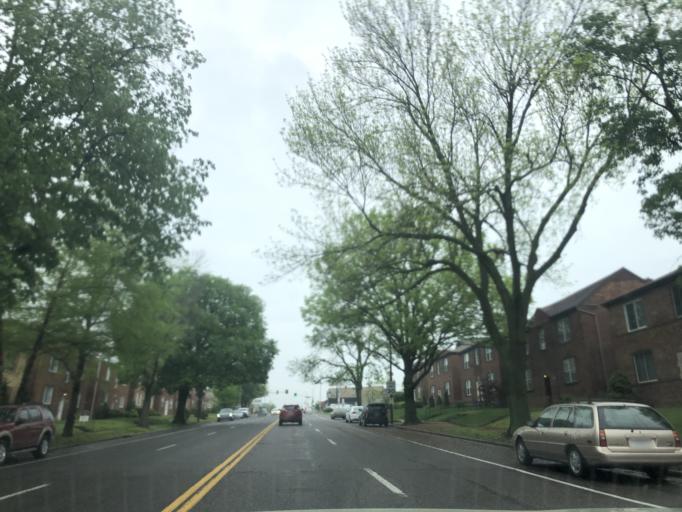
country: US
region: Missouri
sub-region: Saint Louis County
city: Shrewsbury
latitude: 38.5879
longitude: -90.3113
